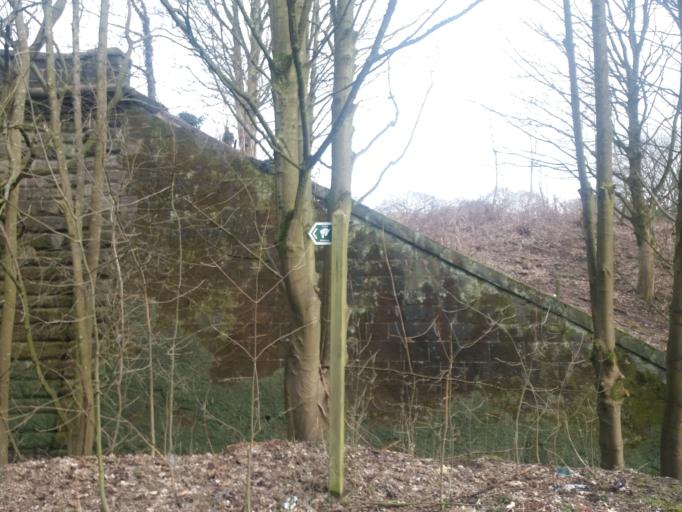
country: GB
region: England
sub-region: Lancashire
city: Chorley
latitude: 53.6510
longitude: -2.6120
